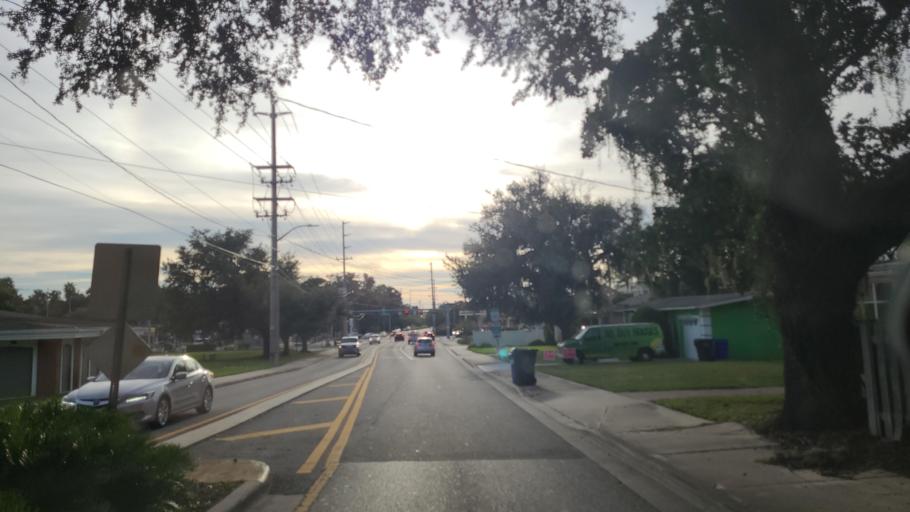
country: US
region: Florida
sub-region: Polk County
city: Lakeland
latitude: 28.0113
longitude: -81.9553
